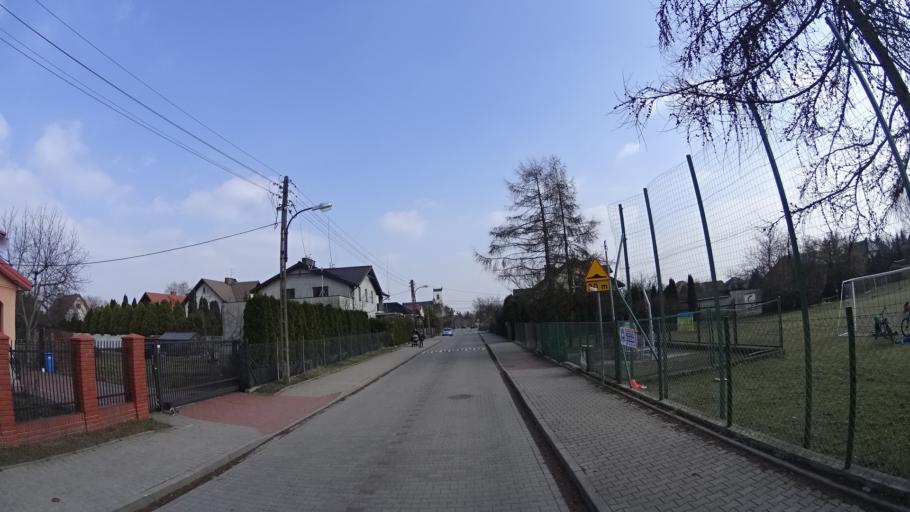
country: PL
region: Masovian Voivodeship
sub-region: Powiat warszawski zachodni
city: Babice
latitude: 52.2445
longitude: 20.8776
